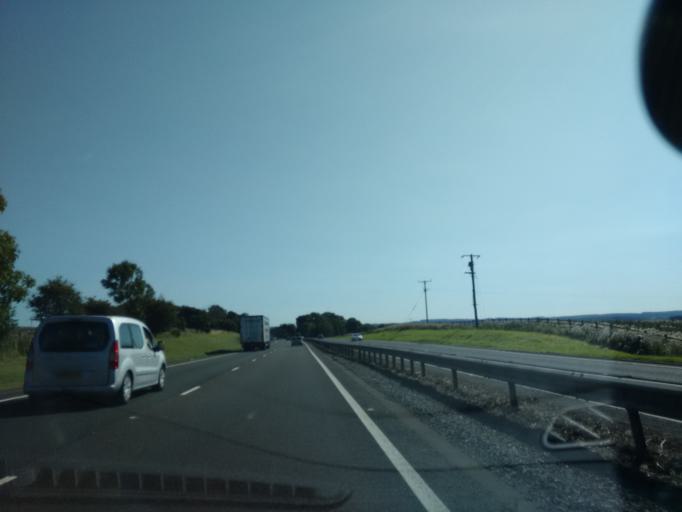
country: GB
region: England
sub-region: Northumberland
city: Corbridge
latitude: 54.9777
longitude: -1.9870
